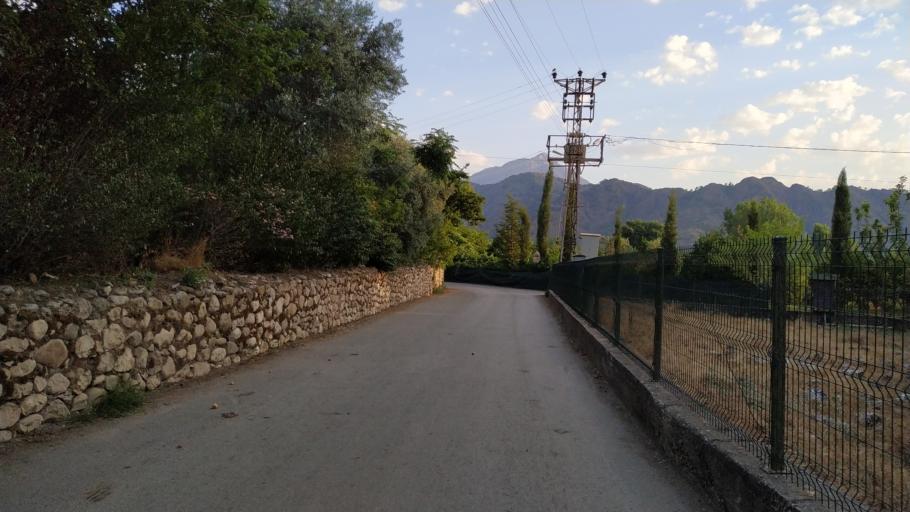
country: TR
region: Antalya
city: Tekirova
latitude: 36.4121
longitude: 30.4753
